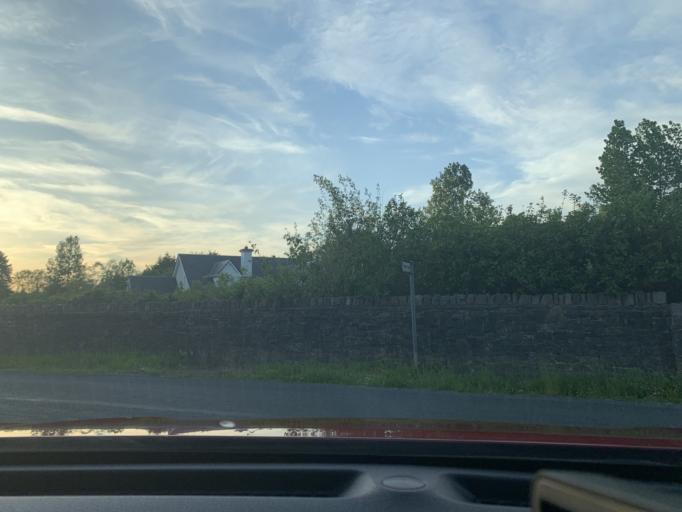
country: IE
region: Connaught
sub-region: Sligo
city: Sligo
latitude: 54.2910
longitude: -8.4306
